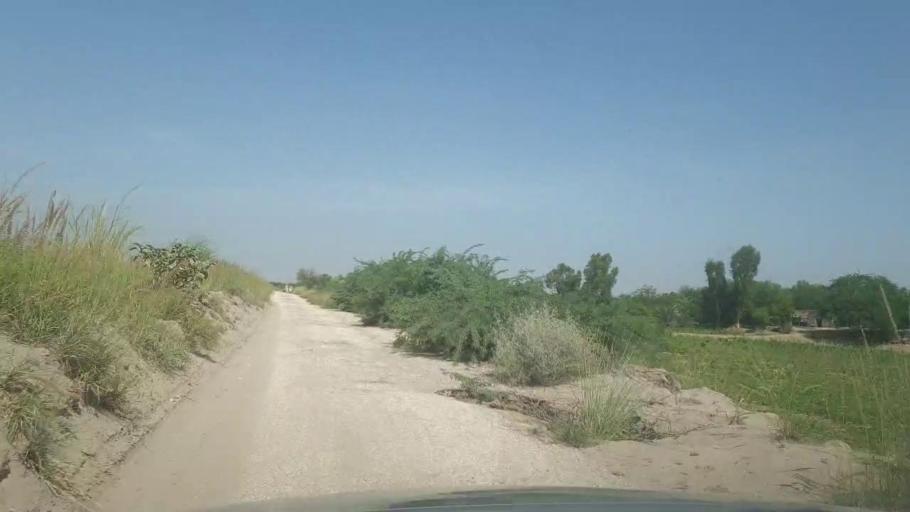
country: PK
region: Sindh
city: Khairpur
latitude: 27.3968
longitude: 69.0696
